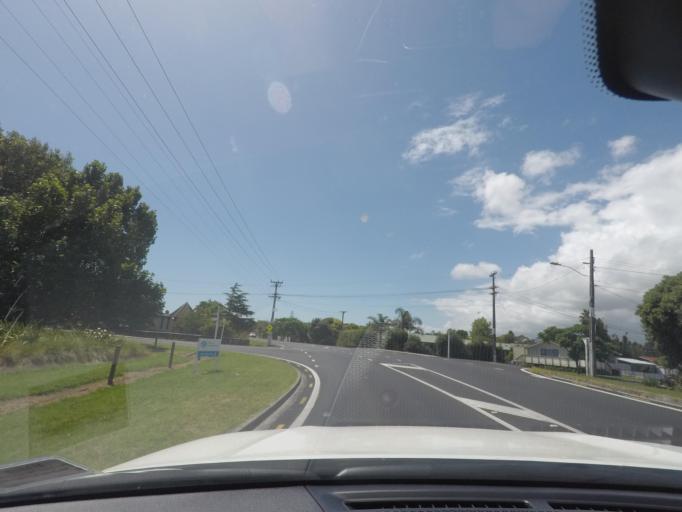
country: NZ
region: Auckland
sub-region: Auckland
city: Parakai
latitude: -36.6637
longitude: 174.4361
